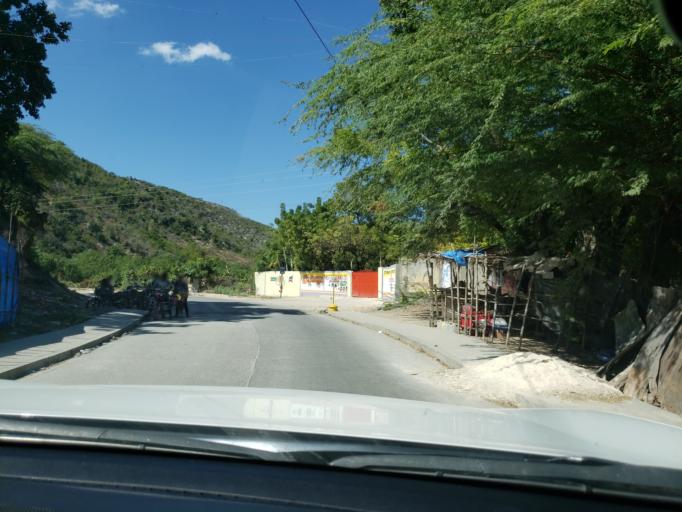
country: HT
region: Nippes
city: Miragoane
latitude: 18.4447
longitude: -73.0998
